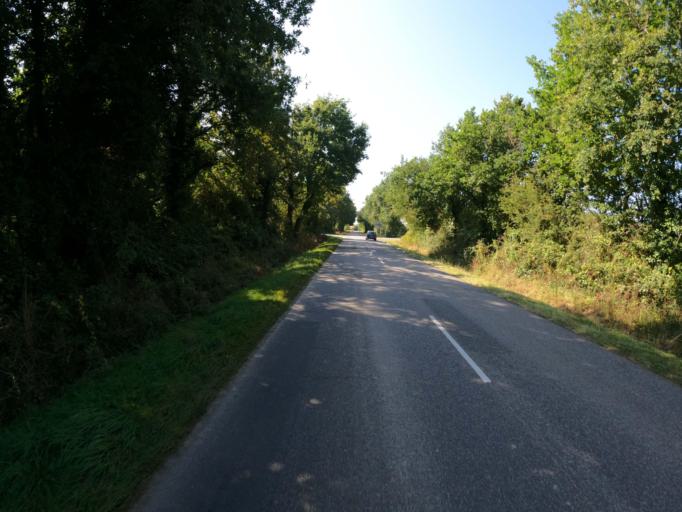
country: FR
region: Pays de la Loire
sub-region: Departement de la Loire-Atlantique
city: La Chevroliere
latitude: 47.0665
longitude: -1.5679
